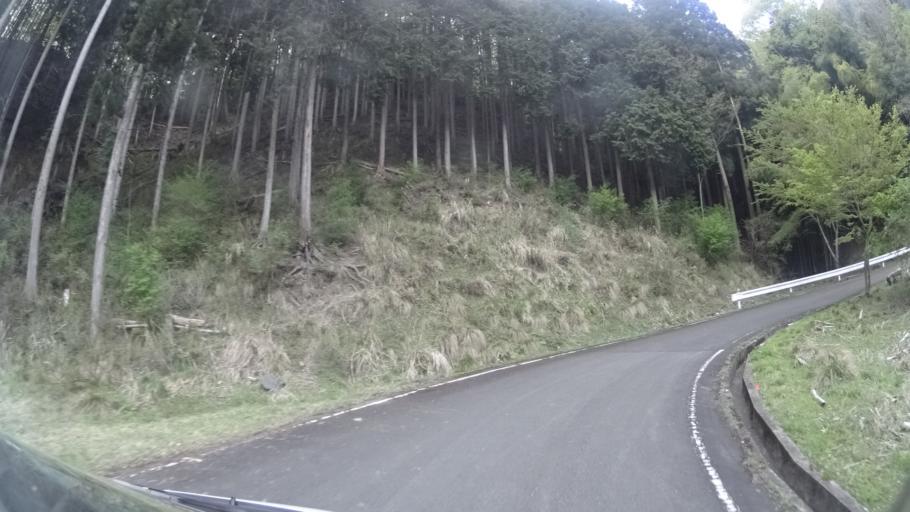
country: JP
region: Kyoto
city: Ayabe
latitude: 35.2576
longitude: 135.3164
